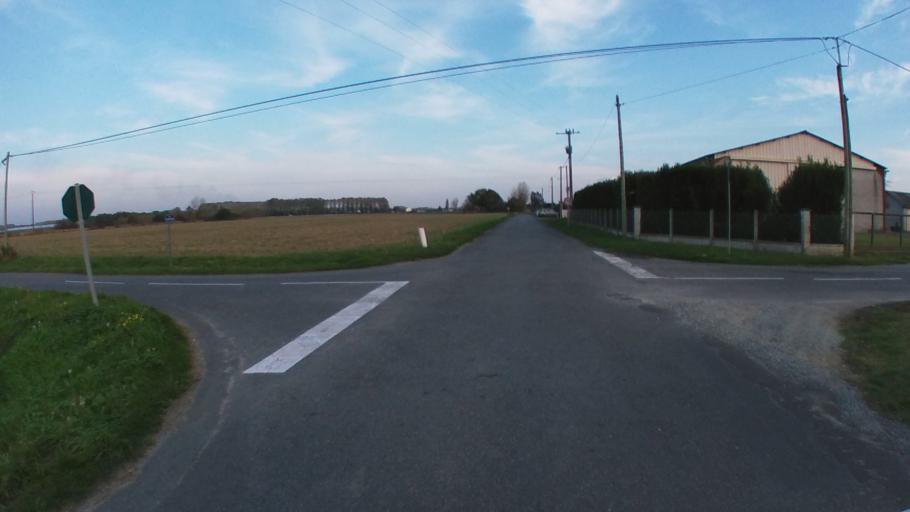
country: FR
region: Pays de la Loire
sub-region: Departement de Maine-et-Loire
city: Vivy
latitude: 47.3107
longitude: -0.0622
